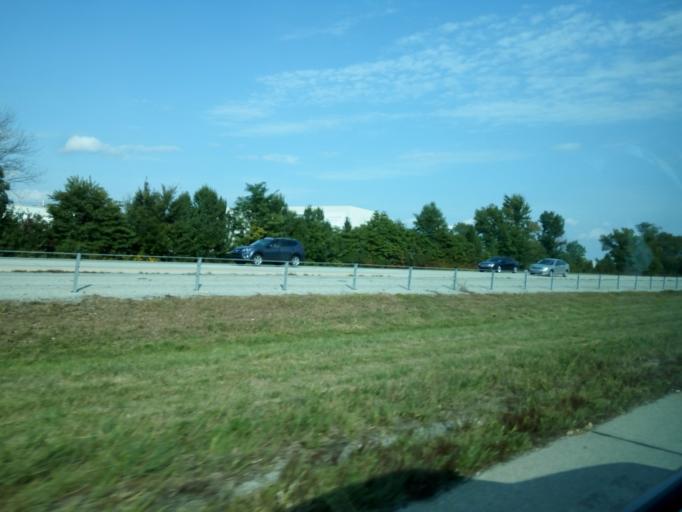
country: US
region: Kentucky
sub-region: Jefferson County
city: Worthington Hills
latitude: 38.2931
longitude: -85.5416
